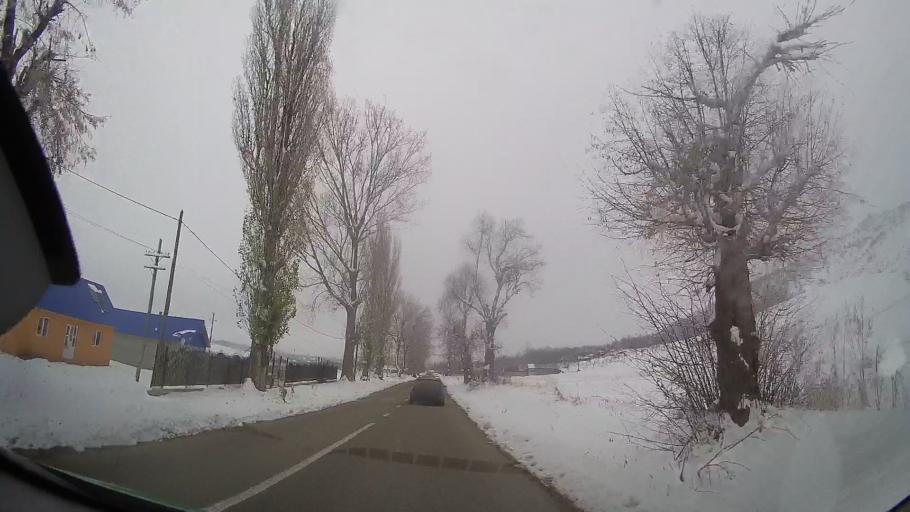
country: RO
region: Neamt
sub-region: Comuna Bozieni
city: Bozieni
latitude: 46.8318
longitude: 27.1758
